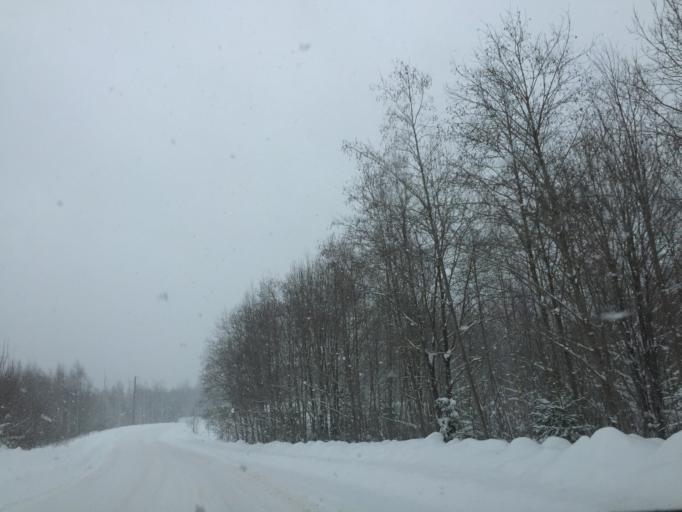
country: LV
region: Amatas Novads
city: Drabesi
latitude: 57.0811
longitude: 25.3441
